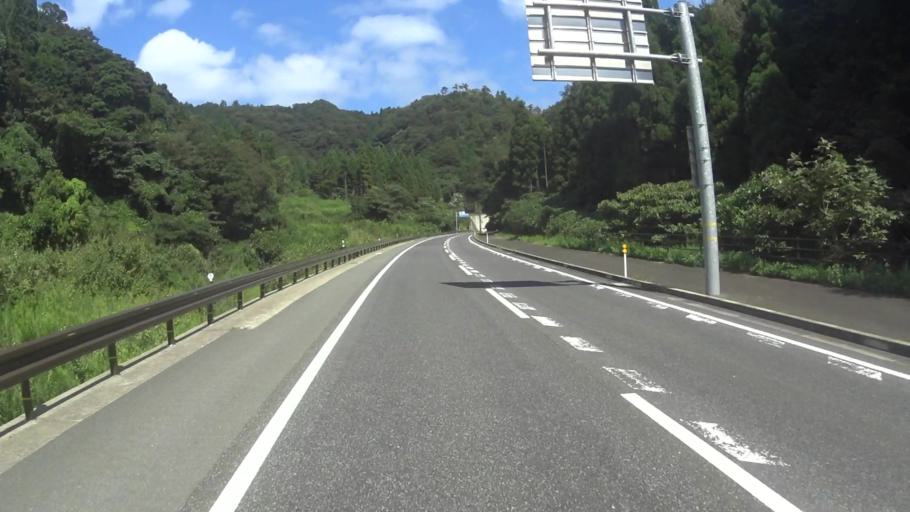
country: JP
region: Kyoto
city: Miyazu
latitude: 35.6761
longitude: 135.2744
